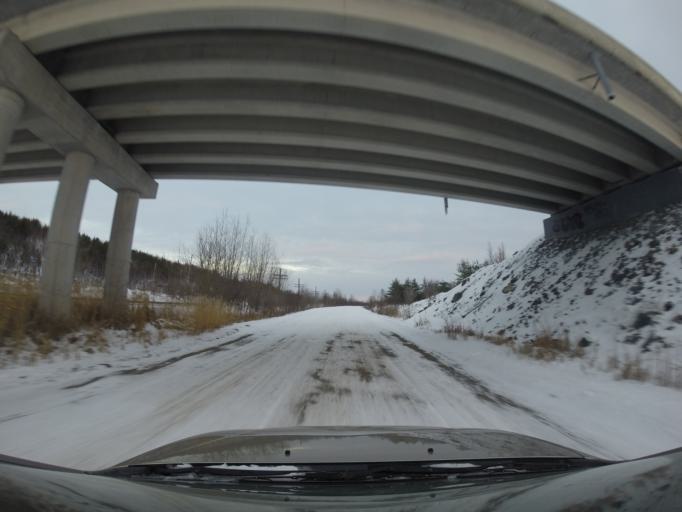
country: CA
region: Ontario
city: Greater Sudbury
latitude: 46.4844
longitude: -80.8795
